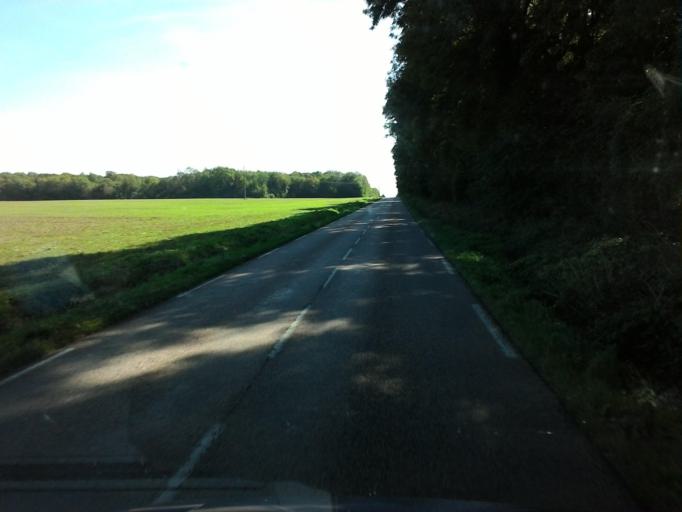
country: FR
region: Bourgogne
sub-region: Departement de l'Yonne
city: Joux-la-Ville
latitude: 47.5914
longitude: 3.8670
